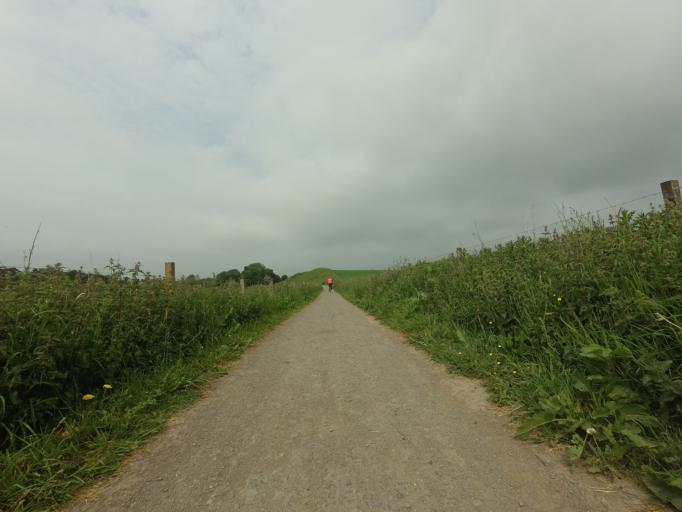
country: GB
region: Scotland
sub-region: Perth and Kinross
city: Milnathort
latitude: 56.2190
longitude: -3.3730
